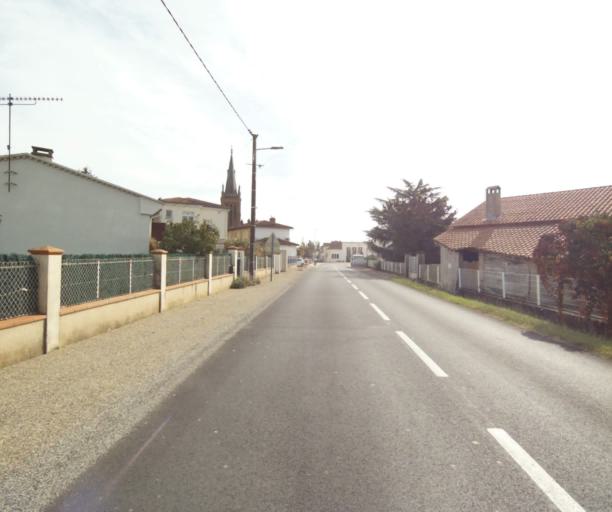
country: FR
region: Midi-Pyrenees
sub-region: Departement du Tarn-et-Garonne
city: Orgueil
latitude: 43.9190
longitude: 1.3977
